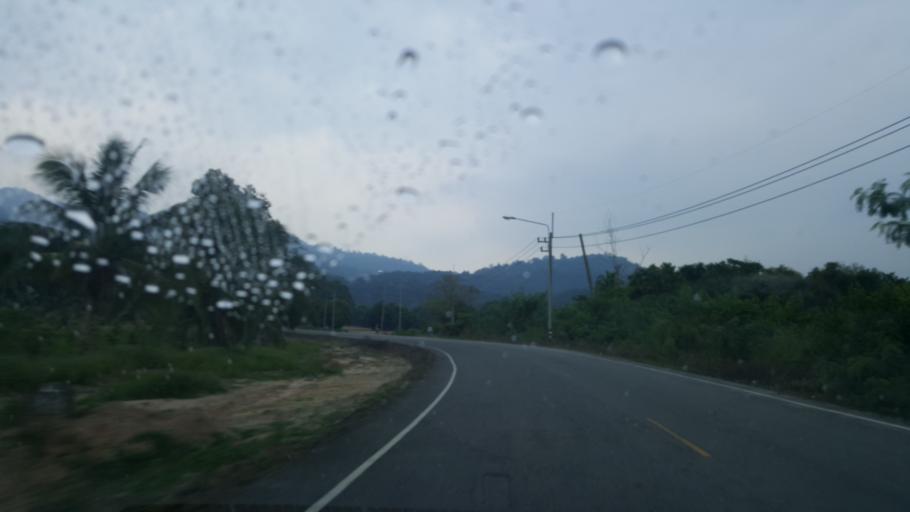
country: TH
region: Chon Buri
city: Ban Bueng
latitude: 13.2371
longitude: 101.0328
